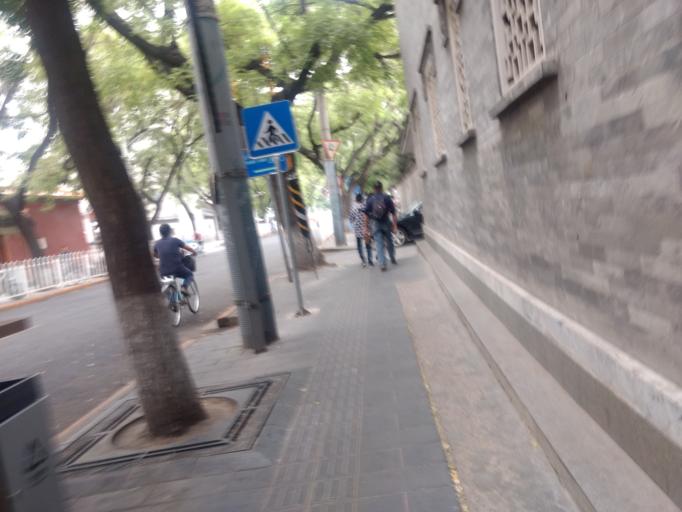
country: CN
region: Beijing
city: Beijing
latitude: 39.9084
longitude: 116.3970
